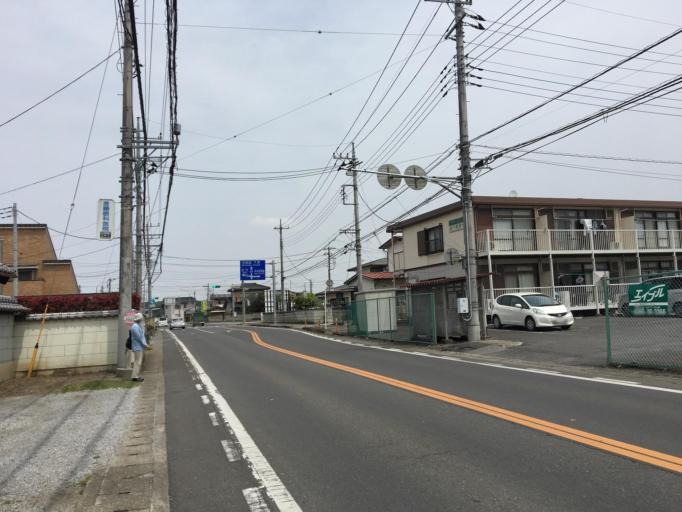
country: JP
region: Tochigi
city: Oyama
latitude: 36.3363
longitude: 139.8175
